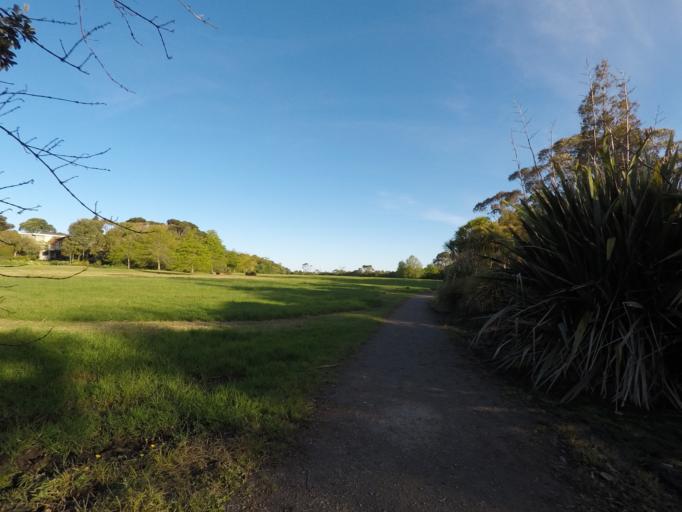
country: NZ
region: Auckland
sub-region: Auckland
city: Rosebank
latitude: -36.8407
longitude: 174.6326
